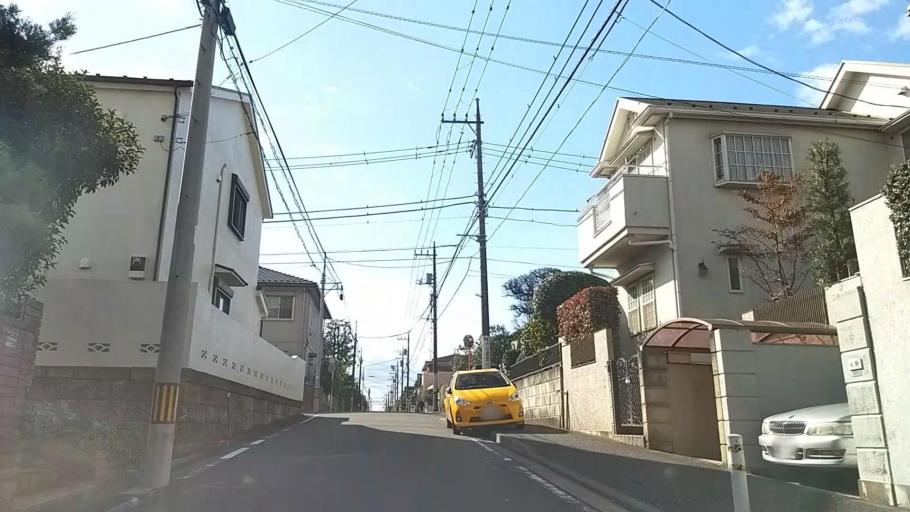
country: JP
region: Kanagawa
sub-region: Kawasaki-shi
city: Kawasaki
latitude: 35.5131
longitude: 139.6661
